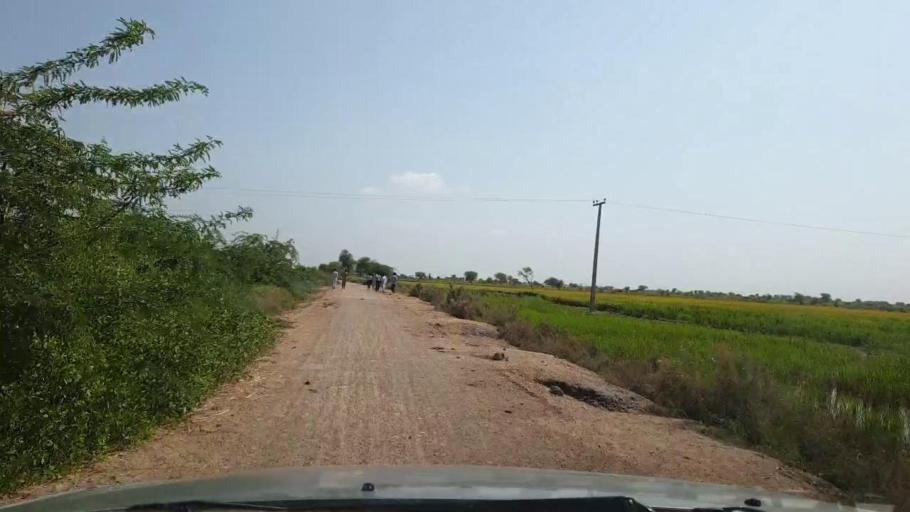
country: PK
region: Sindh
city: Rajo Khanani
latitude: 25.0218
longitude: 68.7980
